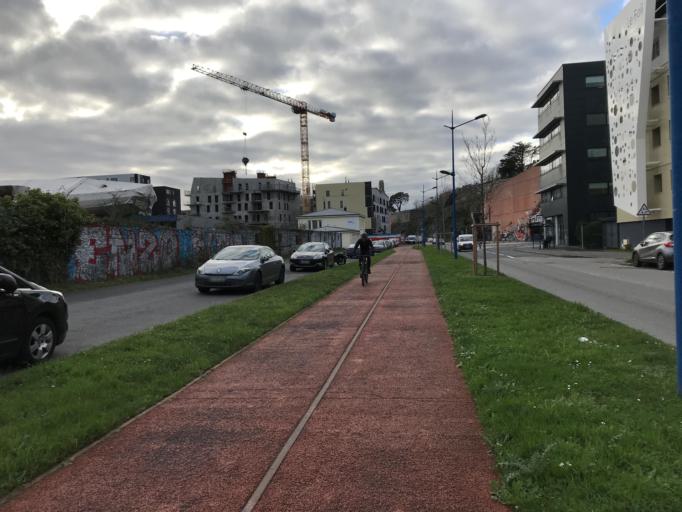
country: FR
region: Brittany
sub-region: Departement du Finistere
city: Brest
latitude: 48.3848
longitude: -4.4798
